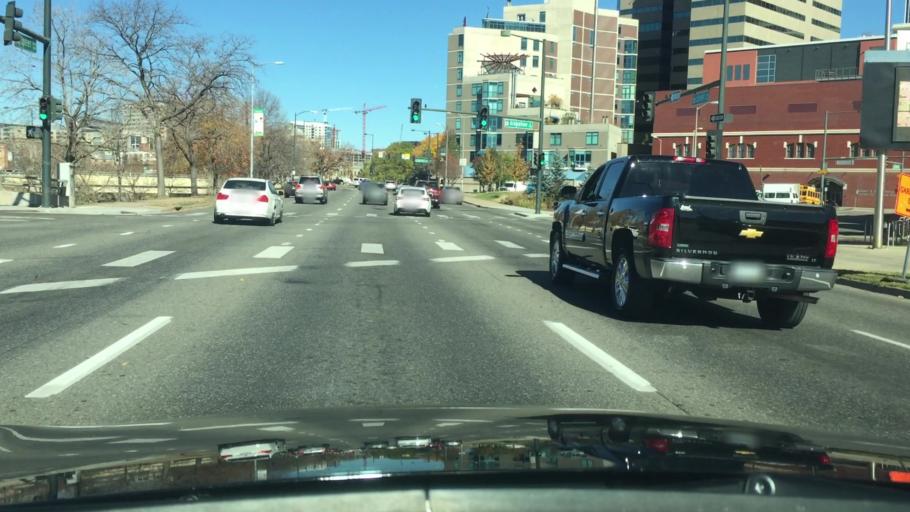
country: US
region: Colorado
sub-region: Denver County
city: Denver
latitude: 39.7442
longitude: -105.0000
